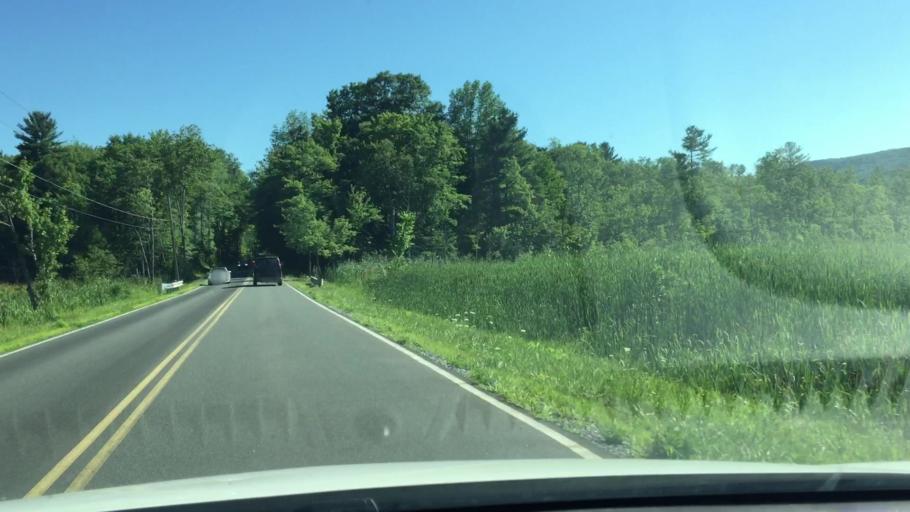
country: US
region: Massachusetts
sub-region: Berkshire County
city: Richmond
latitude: 42.3839
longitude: -73.3432
